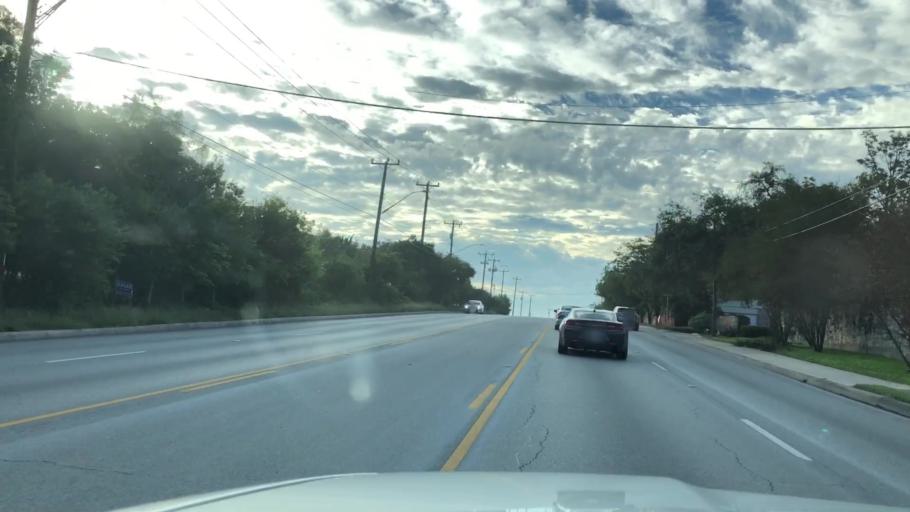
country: US
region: Texas
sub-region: Bexar County
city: Leon Valley
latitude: 29.5316
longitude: -98.6045
